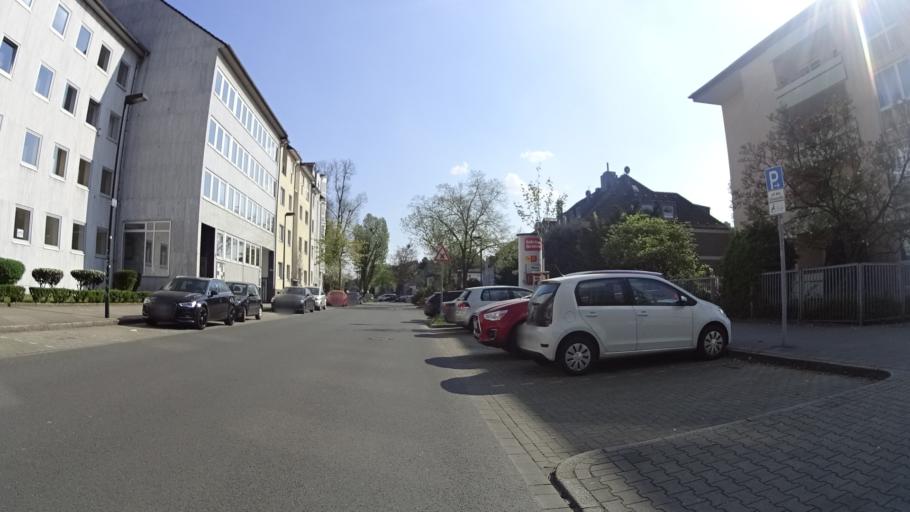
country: DE
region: North Rhine-Westphalia
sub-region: Regierungsbezirk Dusseldorf
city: Dusseldorf
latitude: 51.2056
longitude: 6.7605
